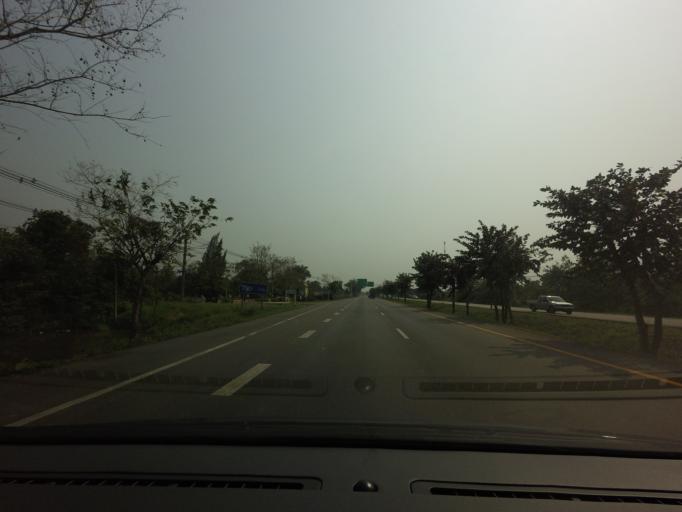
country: TH
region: Prachuap Khiri Khan
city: Kui Buri
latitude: 12.0987
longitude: 99.8538
